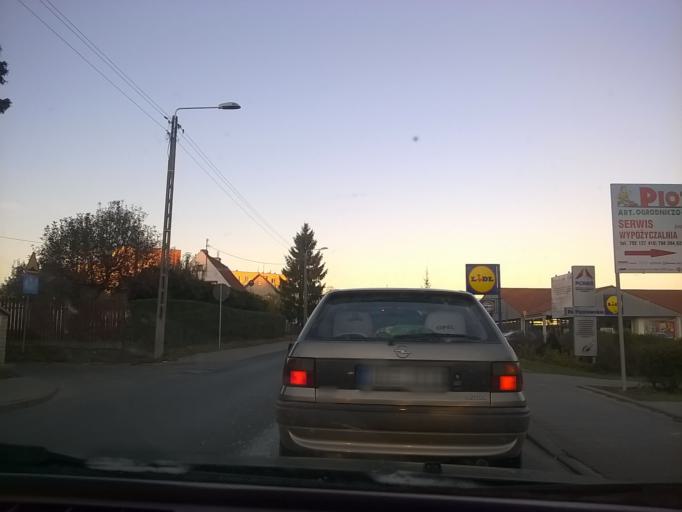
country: PL
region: Warmian-Masurian Voivodeship
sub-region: Powiat ketrzynski
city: Ketrzyn
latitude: 54.0883
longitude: 21.3780
